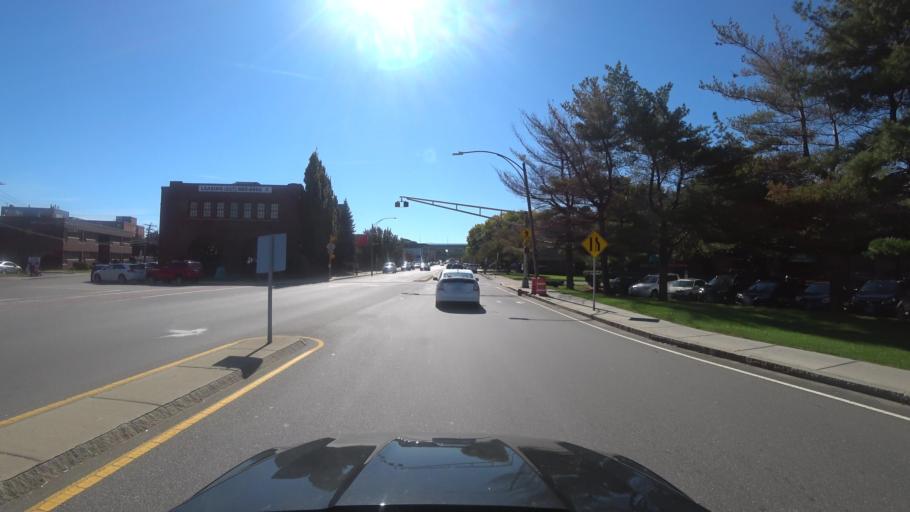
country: US
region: Massachusetts
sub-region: Suffolk County
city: Chelsea
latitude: 42.3950
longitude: -71.0396
